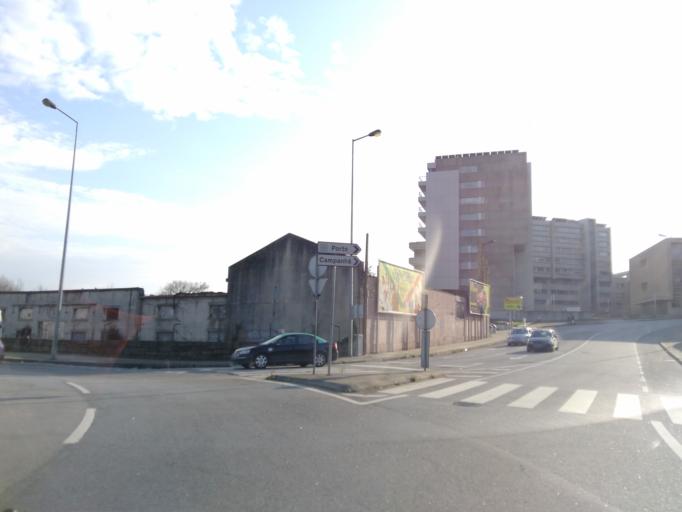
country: PT
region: Porto
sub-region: Gondomar
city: Valbom
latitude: 41.1461
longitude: -8.5795
